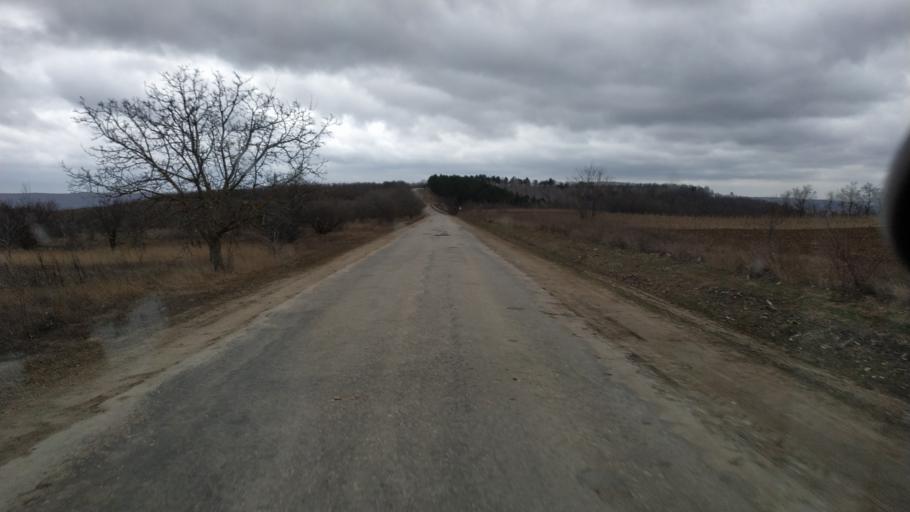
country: MD
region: Calarasi
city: Calarasi
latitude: 47.2213
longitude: 28.2678
